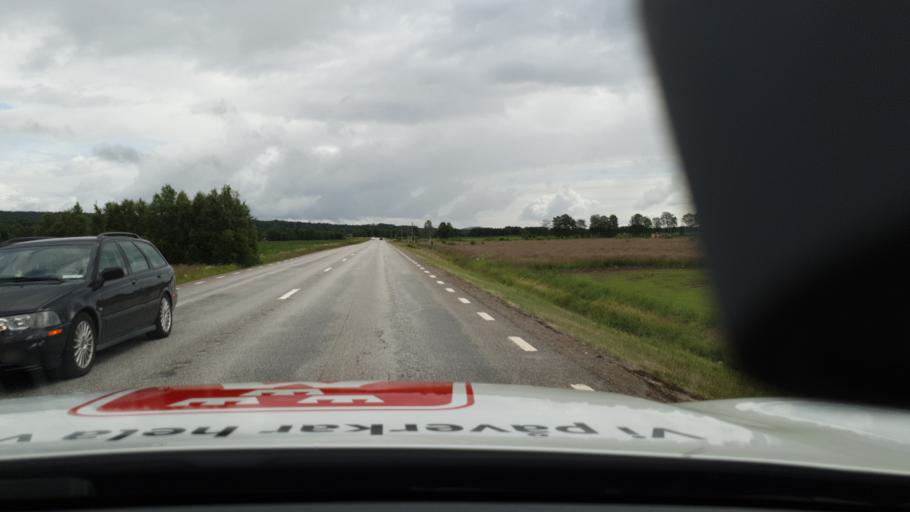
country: SE
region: Norrbotten
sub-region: Pitea Kommun
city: Rosvik
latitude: 65.5735
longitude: 21.7423
